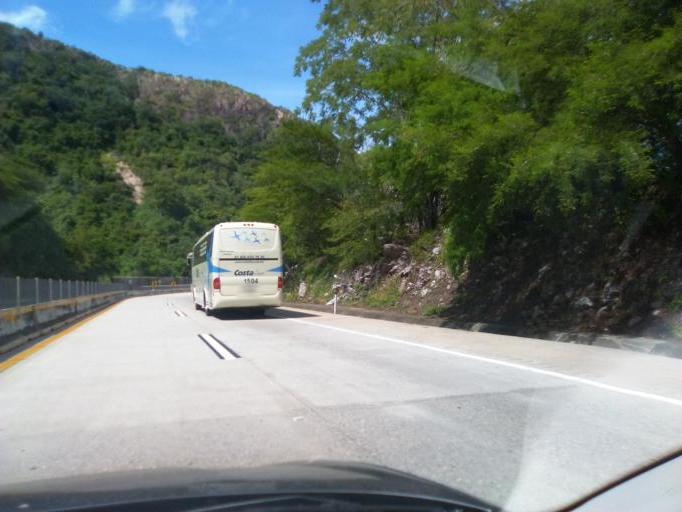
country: MX
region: Guerrero
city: Tierra Colorada
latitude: 17.1199
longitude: -99.5683
